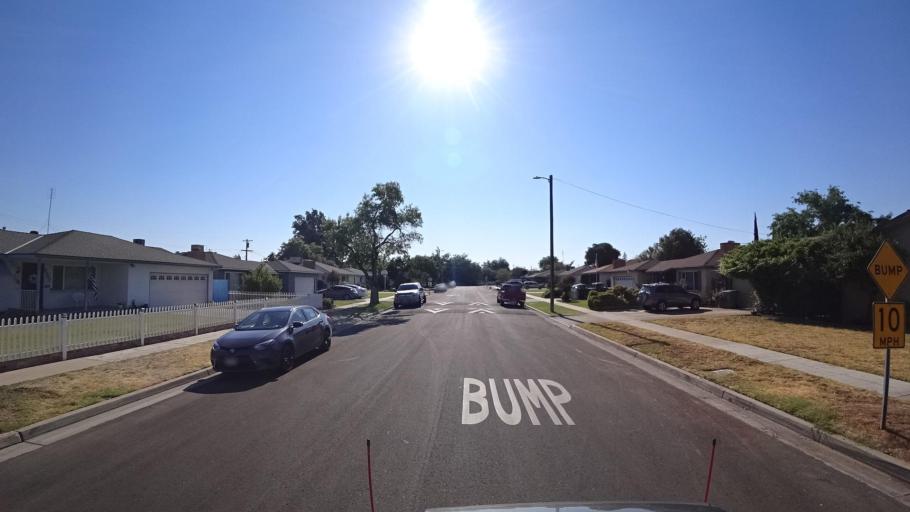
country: US
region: California
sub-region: Fresno County
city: Fresno
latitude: 36.7822
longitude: -119.7570
